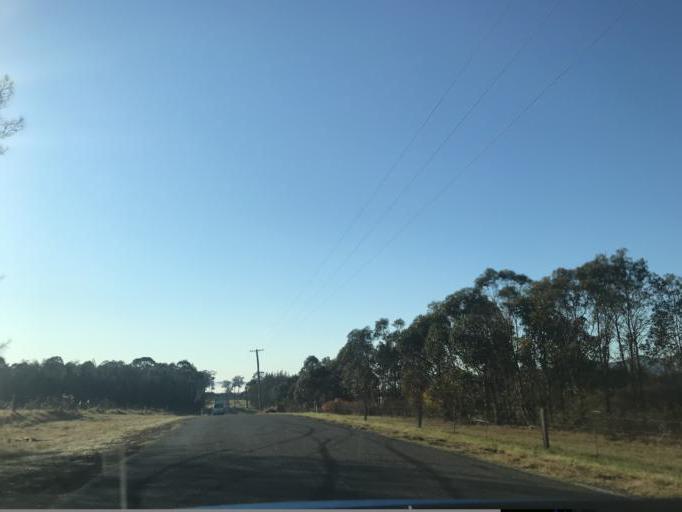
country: AU
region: New South Wales
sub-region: Cessnock
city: Cessnock
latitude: -32.9094
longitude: 151.2933
